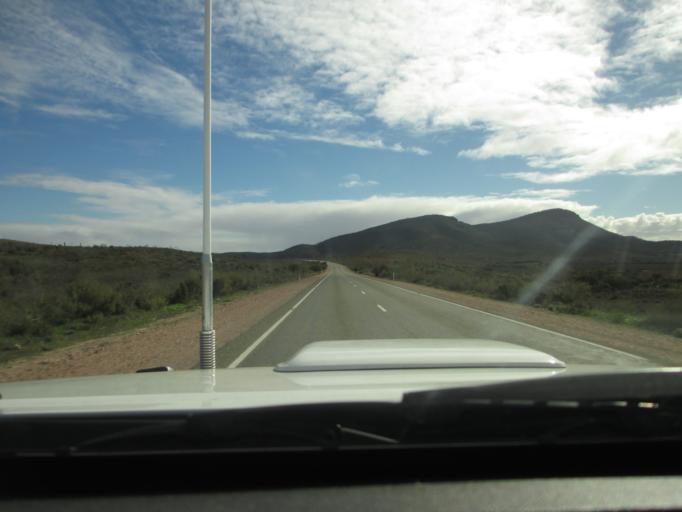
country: AU
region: South Australia
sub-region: Flinders Ranges
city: Quorn
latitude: -31.8025
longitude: 138.3616
